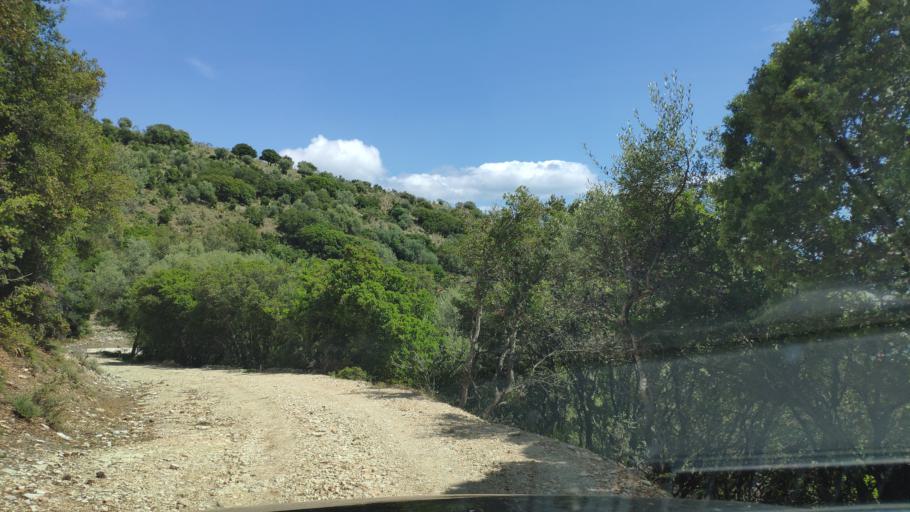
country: AL
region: Vlore
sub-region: Rrethi i Sarandes
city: Konispol
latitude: 39.6368
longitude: 20.2061
